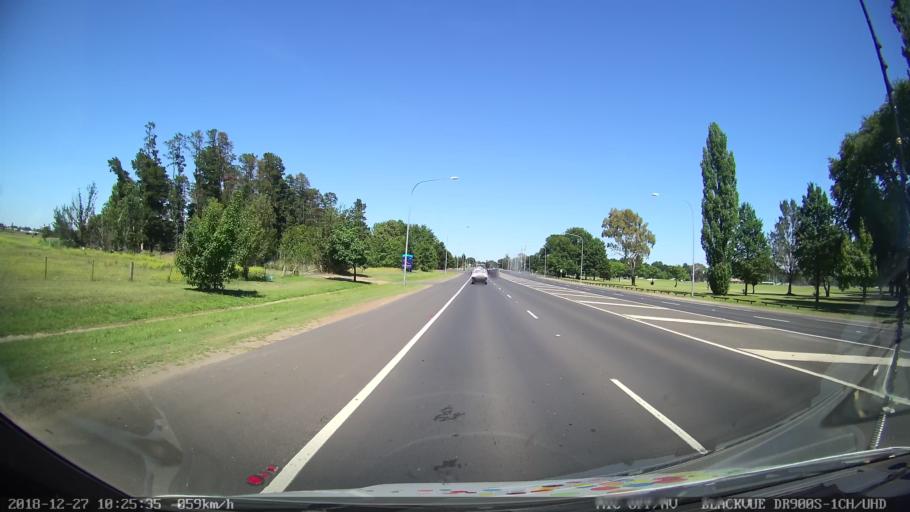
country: AU
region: New South Wales
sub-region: Bathurst Regional
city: Kelso
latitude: -33.4185
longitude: 149.5991
